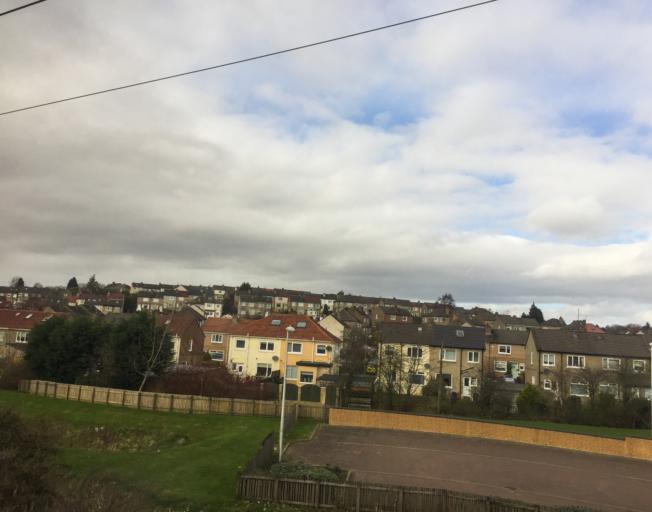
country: GB
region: Scotland
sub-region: East Dunbartonshire
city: Bearsden
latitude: 55.9064
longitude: -4.3416
